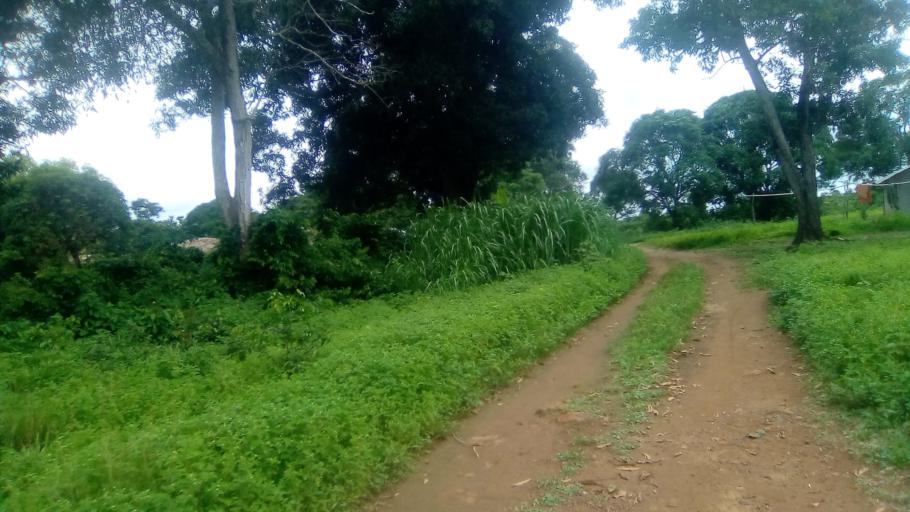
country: SL
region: Southern Province
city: Moyamba
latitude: 8.1570
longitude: -12.4192
